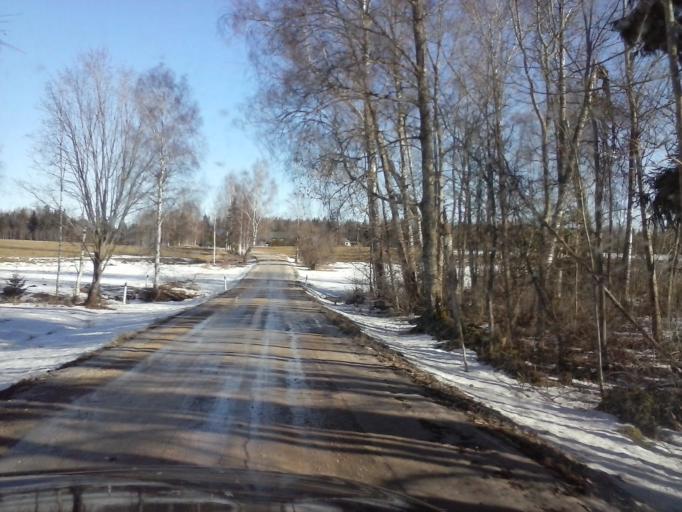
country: EE
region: Laeaene-Virumaa
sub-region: Rakke vald
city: Rakke
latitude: 58.8735
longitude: 26.2768
